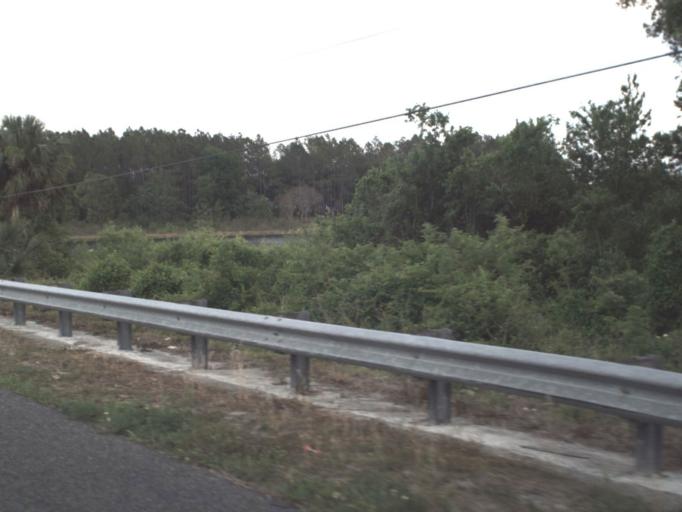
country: US
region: Florida
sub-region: Lake County
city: Umatilla
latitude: 28.9039
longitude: -81.6829
